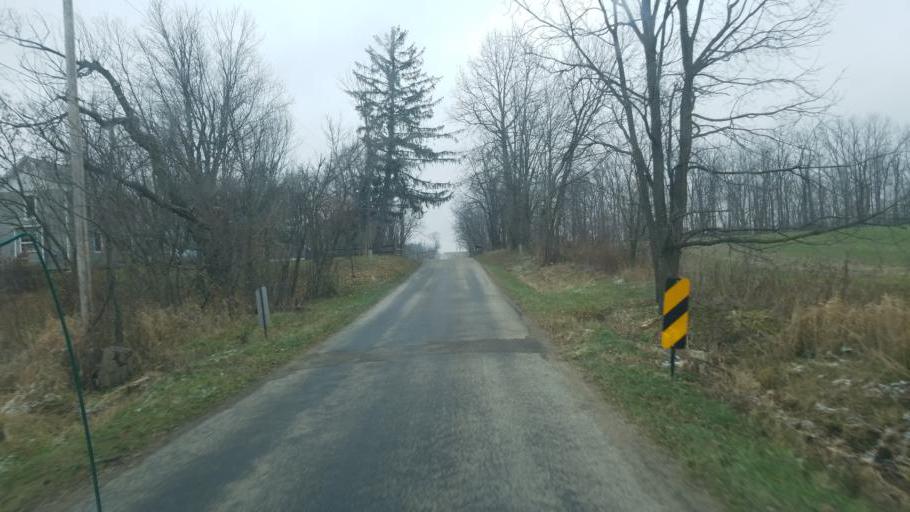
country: US
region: Ohio
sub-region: Huron County
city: New London
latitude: 41.0381
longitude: -82.3259
